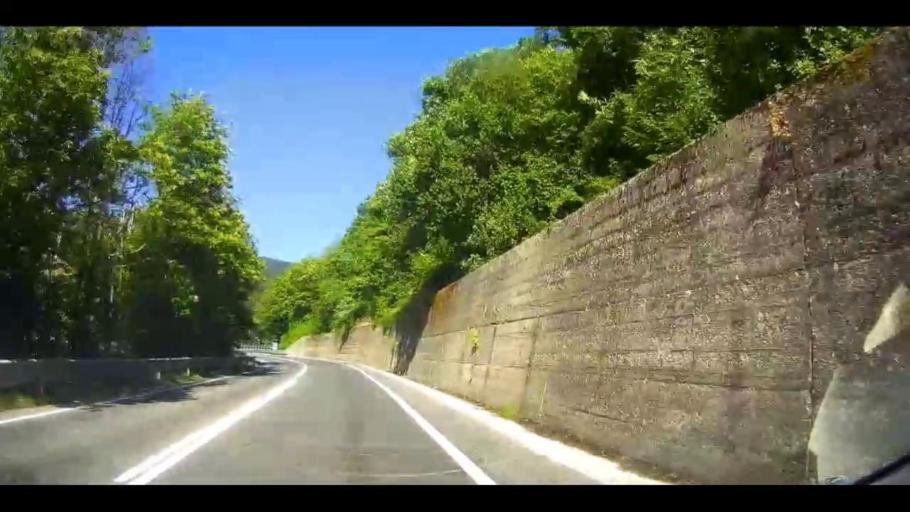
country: IT
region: Calabria
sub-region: Provincia di Cosenza
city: Celico
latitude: 39.3173
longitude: 16.3608
